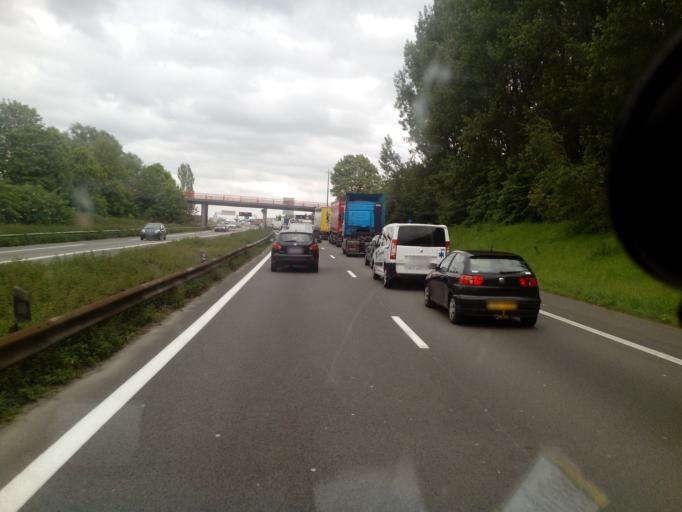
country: FR
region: Nord-Pas-de-Calais
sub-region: Departement du Nord
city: Ennetieres-en-Weppes
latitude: 50.6372
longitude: 2.9416
